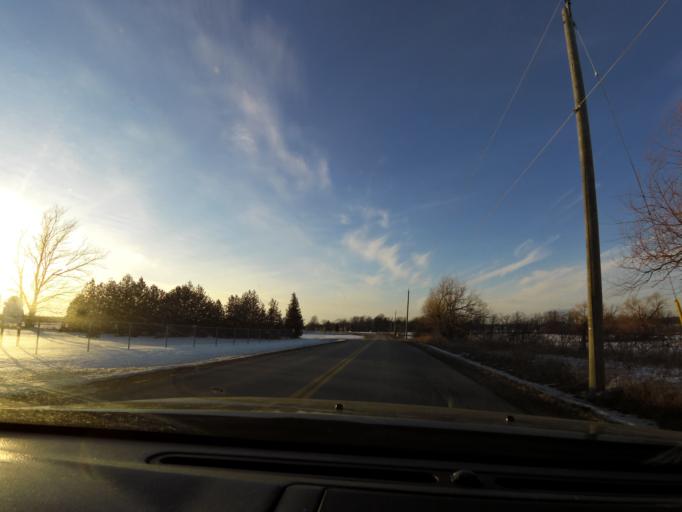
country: CA
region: Ontario
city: Hamilton
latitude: 43.1149
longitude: -79.6500
